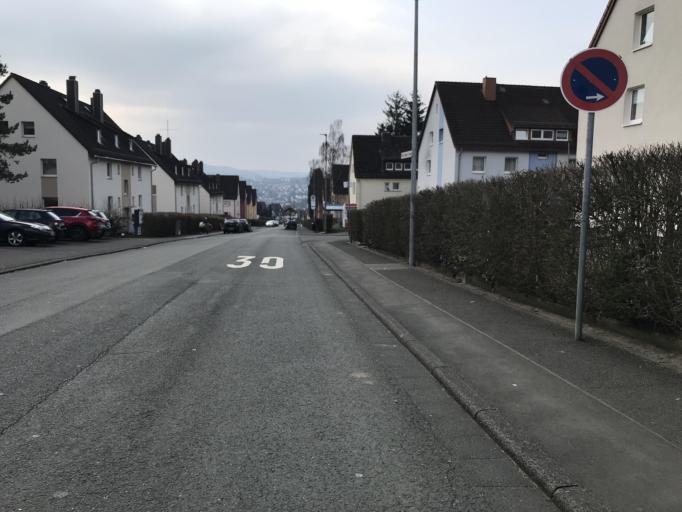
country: DE
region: Hesse
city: Herborn
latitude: 50.6927
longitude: 8.3143
